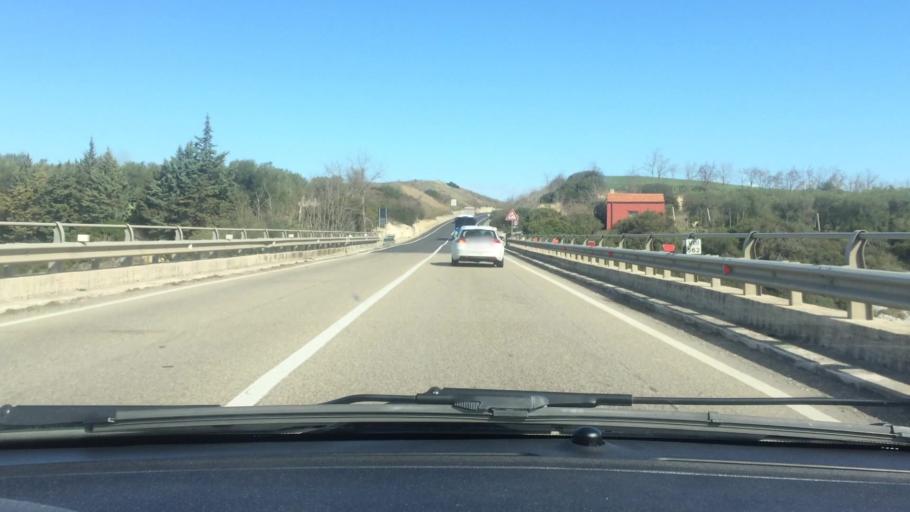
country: IT
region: Basilicate
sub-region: Provincia di Matera
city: La Martella
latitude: 40.5987
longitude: 16.5659
